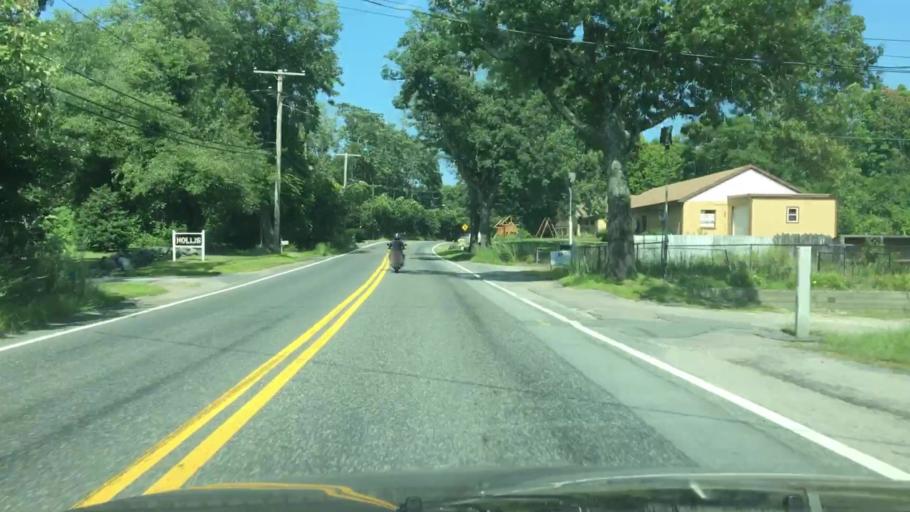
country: US
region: Massachusetts
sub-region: Middlesex County
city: Holliston
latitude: 42.1810
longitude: -71.4471
